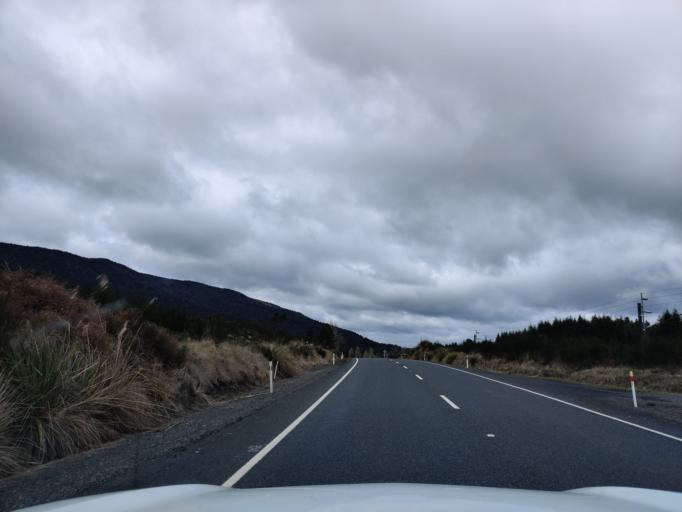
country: NZ
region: Manawatu-Wanganui
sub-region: Ruapehu District
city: Waiouru
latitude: -39.2065
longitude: 175.4025
